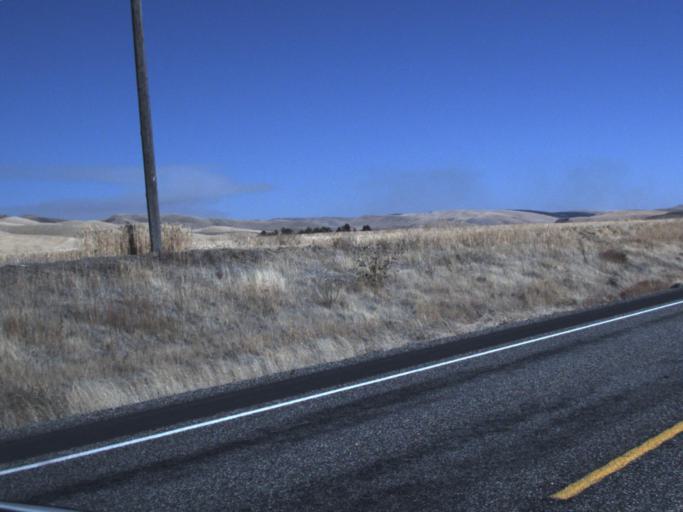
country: US
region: Washington
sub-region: Walla Walla County
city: Waitsburg
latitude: 46.2991
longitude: -118.3481
